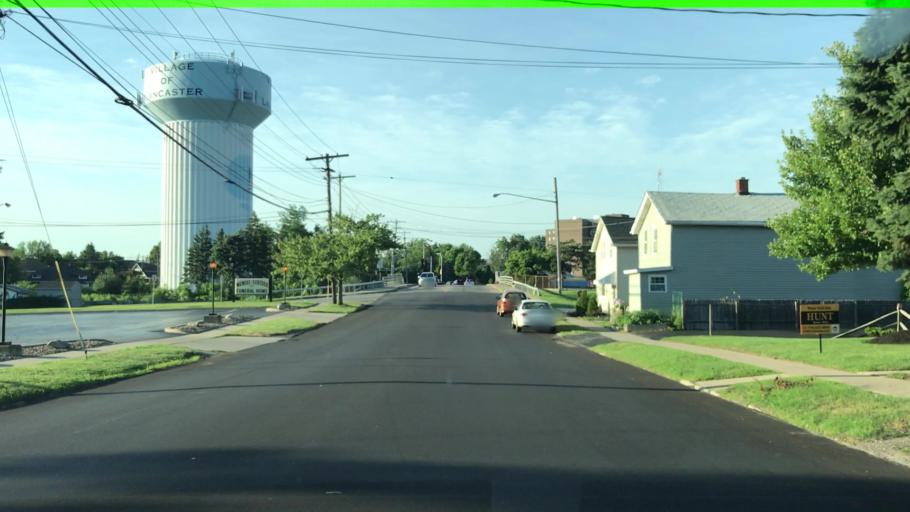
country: US
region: New York
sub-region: Erie County
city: Lancaster
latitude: 42.9002
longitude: -78.6737
